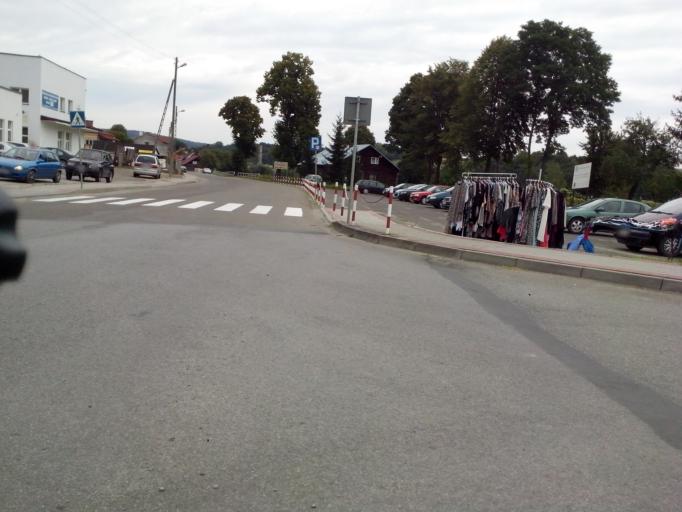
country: PL
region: Subcarpathian Voivodeship
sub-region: Powiat brzozowski
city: Jasienica Rosielna
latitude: 49.7511
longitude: 21.9420
